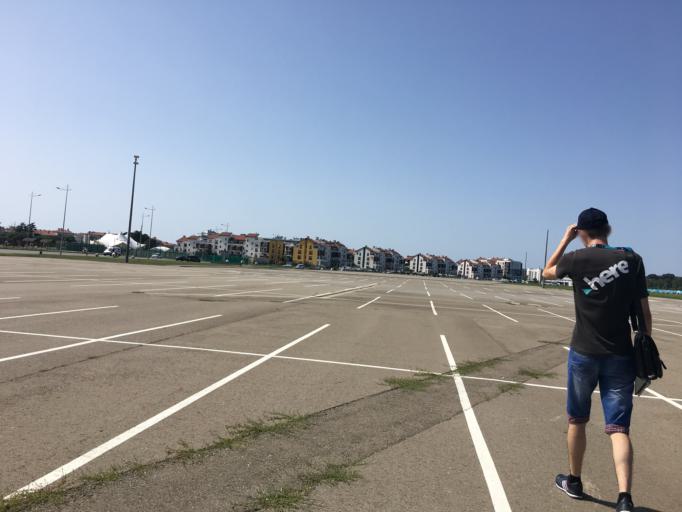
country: RU
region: Krasnodarskiy
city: Adler
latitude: 43.4119
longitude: 39.9480
